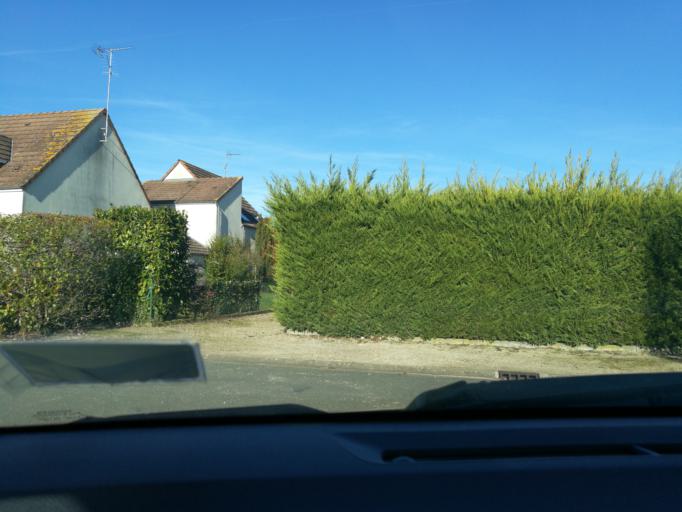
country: FR
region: Centre
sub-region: Departement du Loiret
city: Chaingy
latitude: 47.8834
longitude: 1.7770
